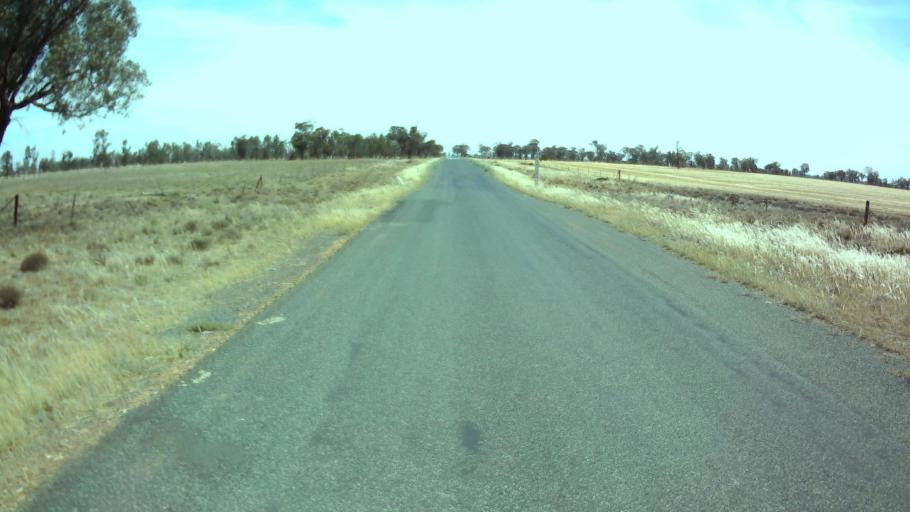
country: AU
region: New South Wales
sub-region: Weddin
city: Grenfell
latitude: -33.9967
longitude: 147.7749
